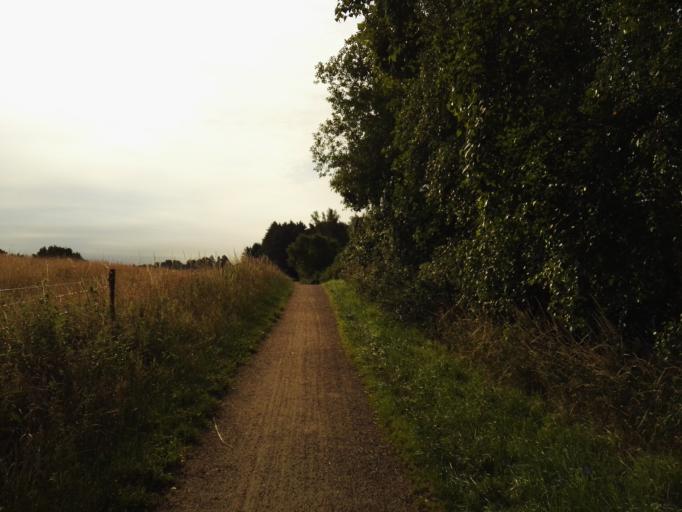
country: DK
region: Capital Region
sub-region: Ballerup Kommune
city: Ballerup
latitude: 55.7504
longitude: 12.3560
